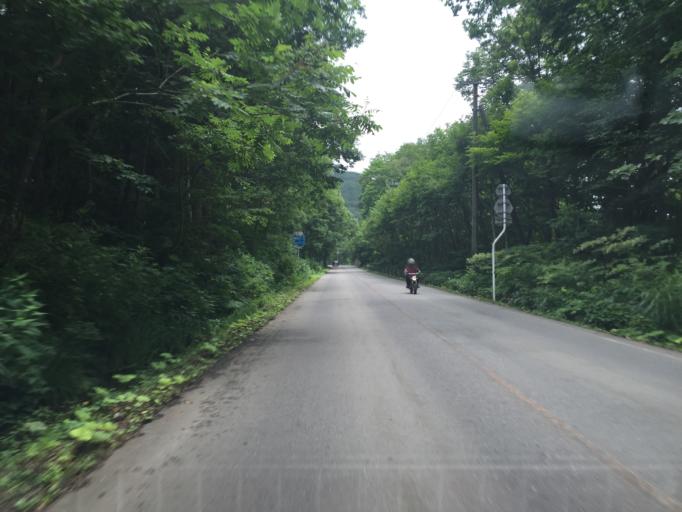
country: JP
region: Fukushima
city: Inawashiro
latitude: 37.7089
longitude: 140.0628
